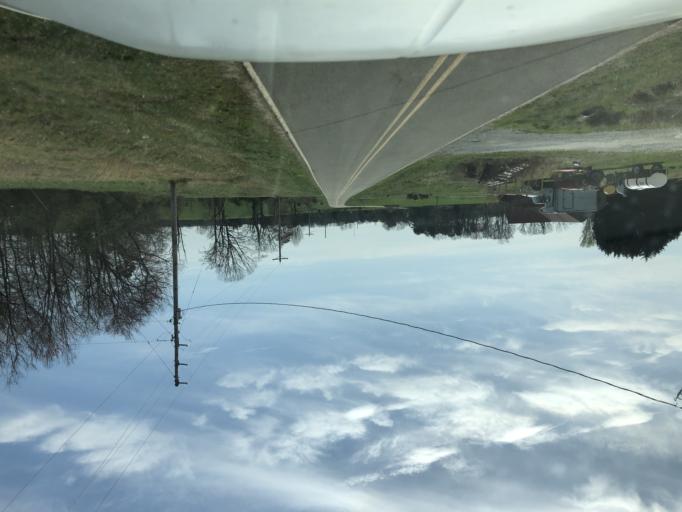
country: US
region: North Carolina
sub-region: Cleveland County
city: Shelby
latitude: 35.4773
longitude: -81.6413
